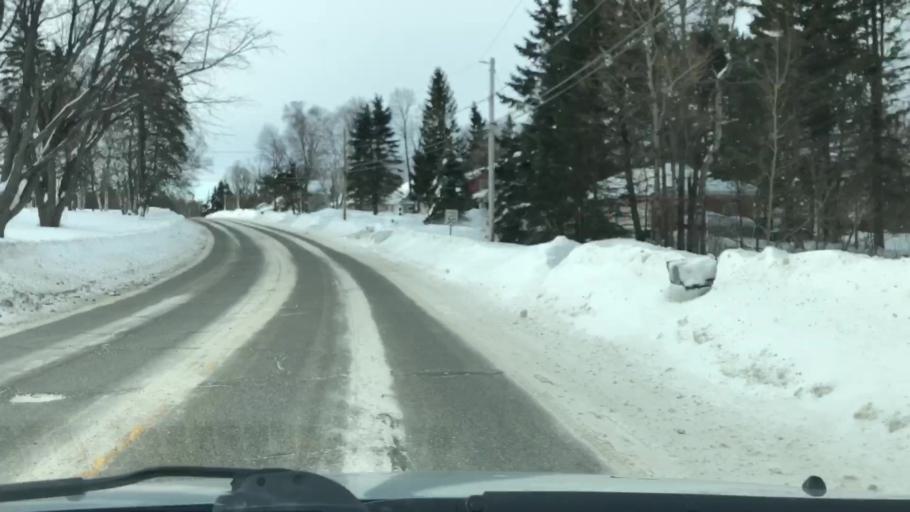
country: US
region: Minnesota
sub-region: Saint Louis County
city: Duluth
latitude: 46.7970
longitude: -92.1492
